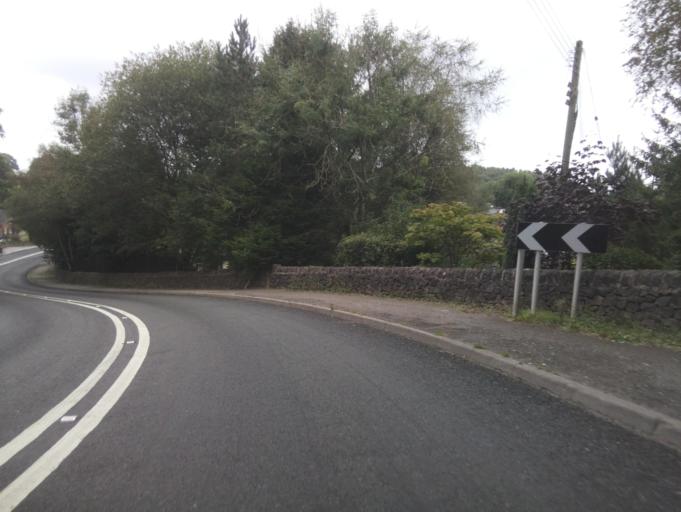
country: GB
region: England
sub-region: Staffordshire
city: Cheadle
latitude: 53.0214
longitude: -1.9466
